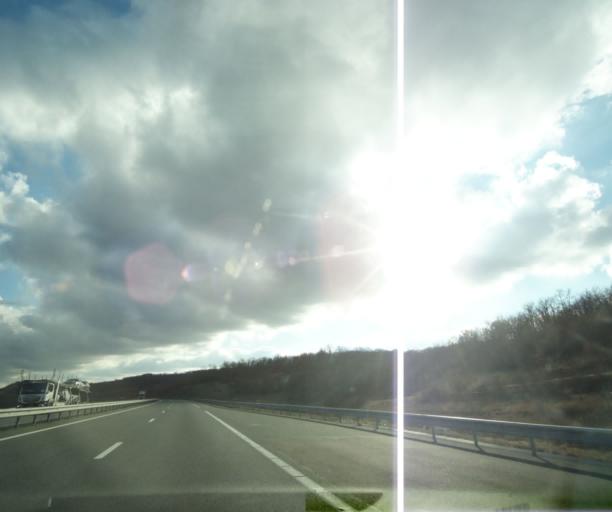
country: FR
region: Midi-Pyrenees
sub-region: Departement du Lot
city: Le Vigan
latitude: 44.7326
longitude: 1.5559
